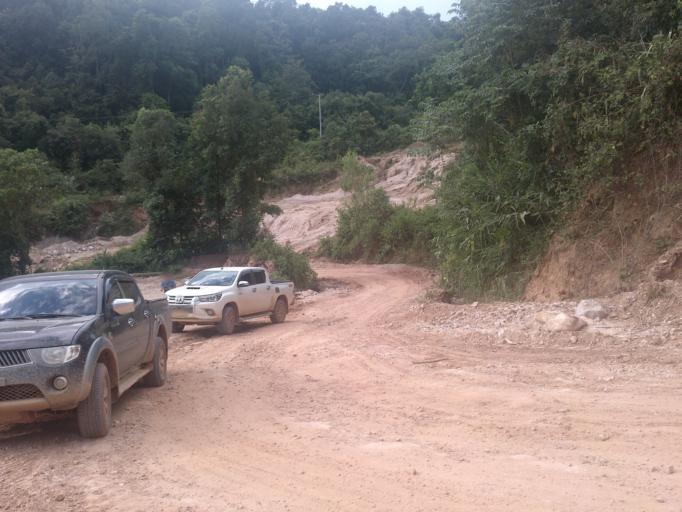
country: LA
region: Phongsali
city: Phongsali
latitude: 21.3322
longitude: 102.0535
